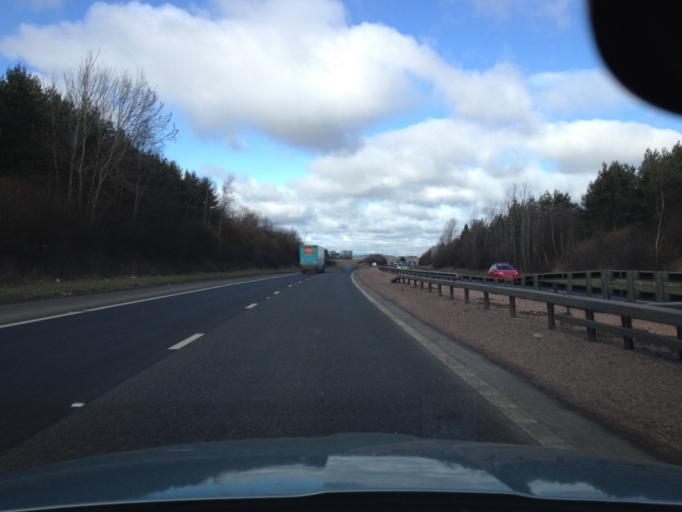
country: GB
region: Scotland
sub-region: Edinburgh
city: Balerno
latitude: 55.9215
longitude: -3.3425
